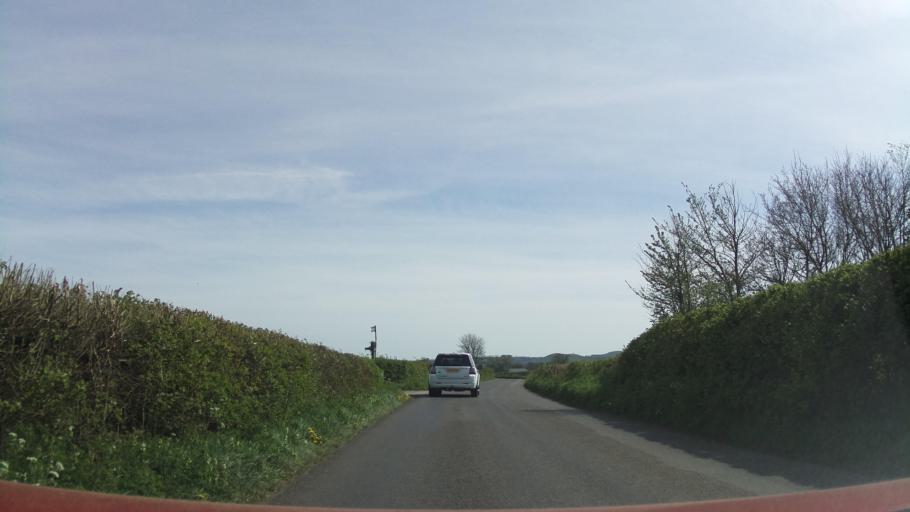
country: GB
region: England
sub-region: Somerset
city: Yeovil
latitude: 51.0174
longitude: -2.5934
